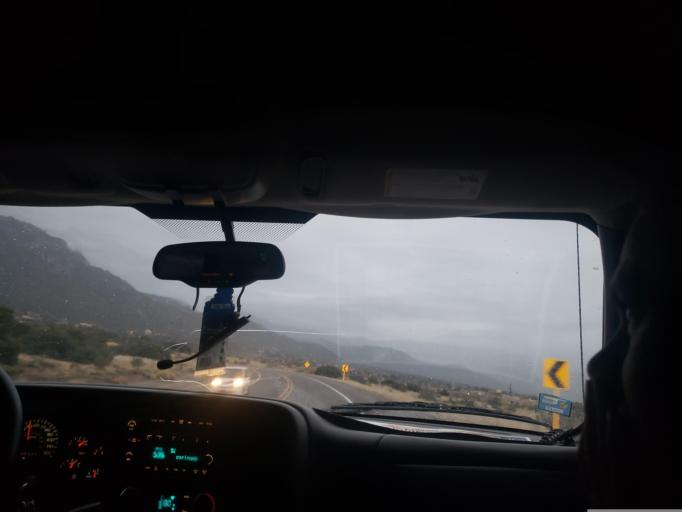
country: US
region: New Mexico
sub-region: Bernalillo County
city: Sandia Heights
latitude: 35.1961
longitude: -106.5018
